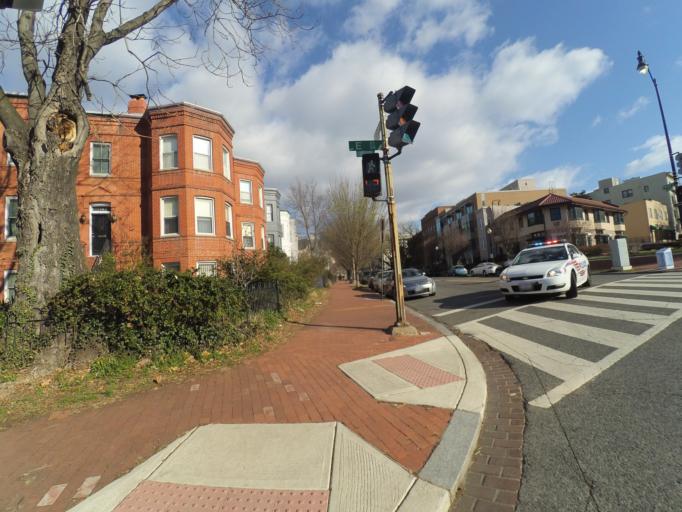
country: US
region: Washington, D.C.
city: Washington, D.C.
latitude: 38.8835
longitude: -77.0060
